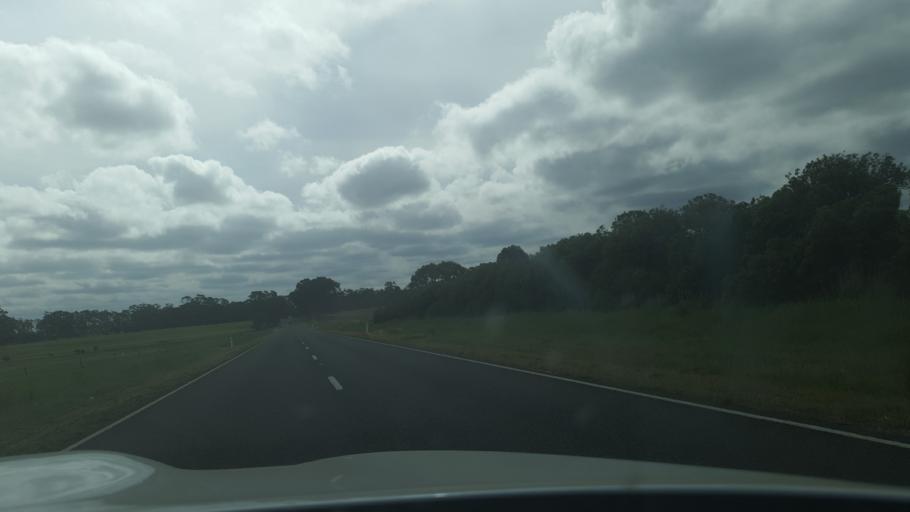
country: AU
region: Victoria
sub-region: Central Goldfields
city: Maryborough
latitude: -37.2064
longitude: 143.7148
